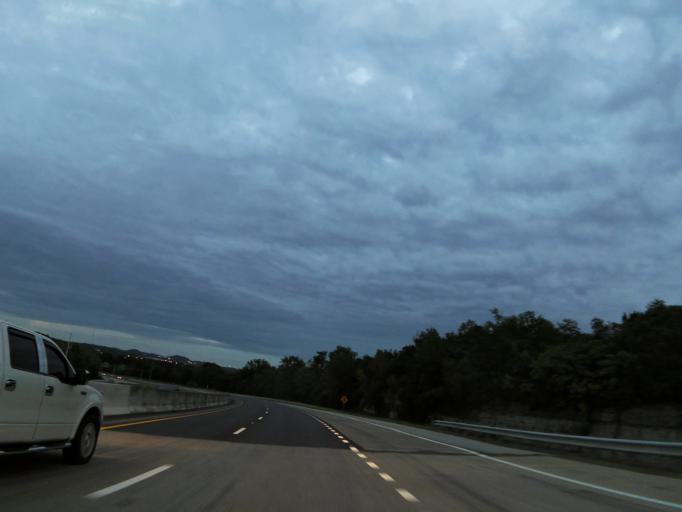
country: US
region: Tennessee
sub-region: Davidson County
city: Nashville
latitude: 36.2289
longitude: -86.8342
